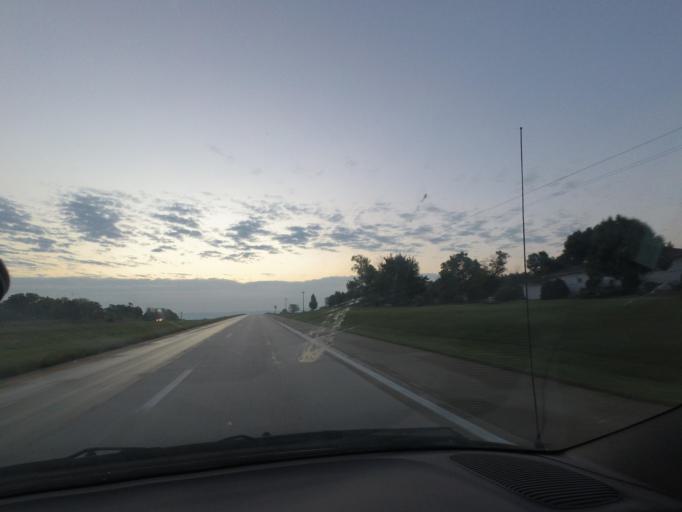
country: US
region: Missouri
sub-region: Macon County
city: Macon
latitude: 39.7592
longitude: -92.6679
